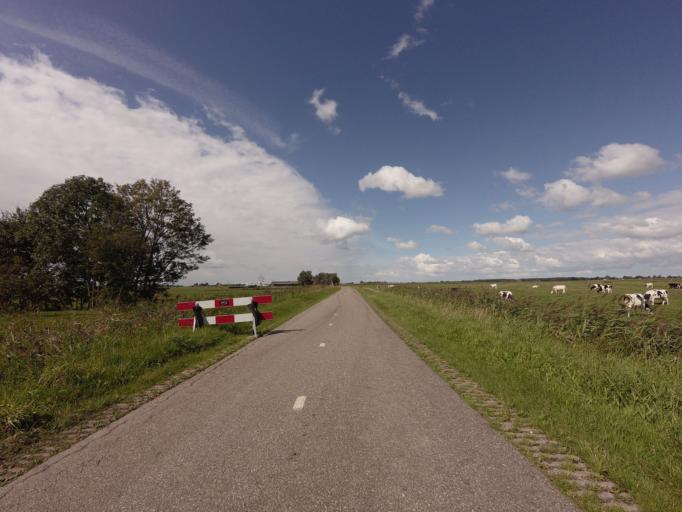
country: NL
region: Friesland
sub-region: Sudwest Fryslan
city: IJlst
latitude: 53.0282
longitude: 5.5722
